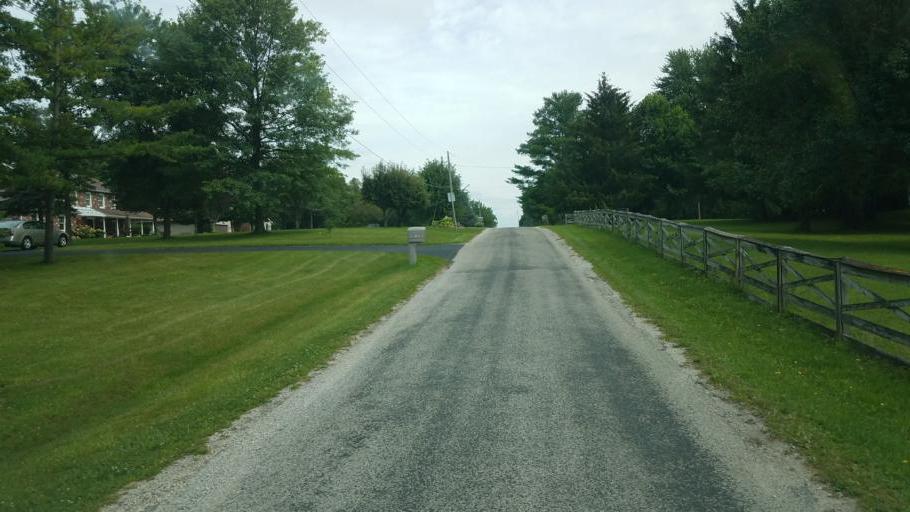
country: US
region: Ohio
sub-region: Marion County
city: Marion
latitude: 40.5141
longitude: -83.0338
